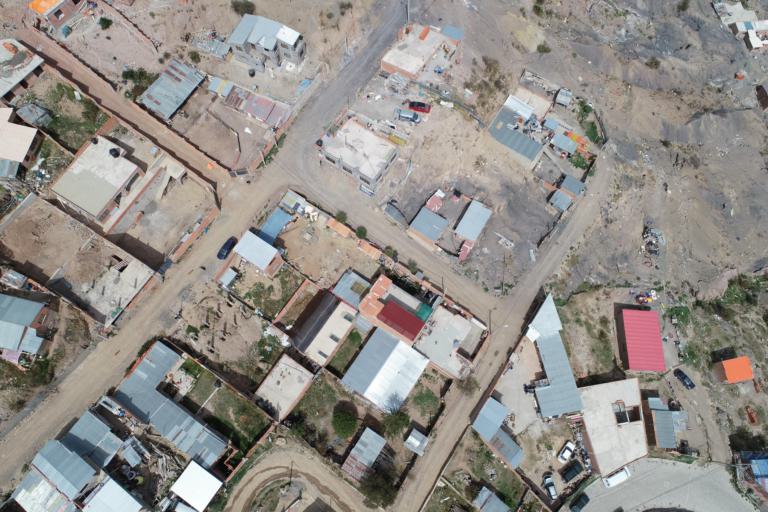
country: BO
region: La Paz
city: La Paz
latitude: -16.5534
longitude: -68.0525
